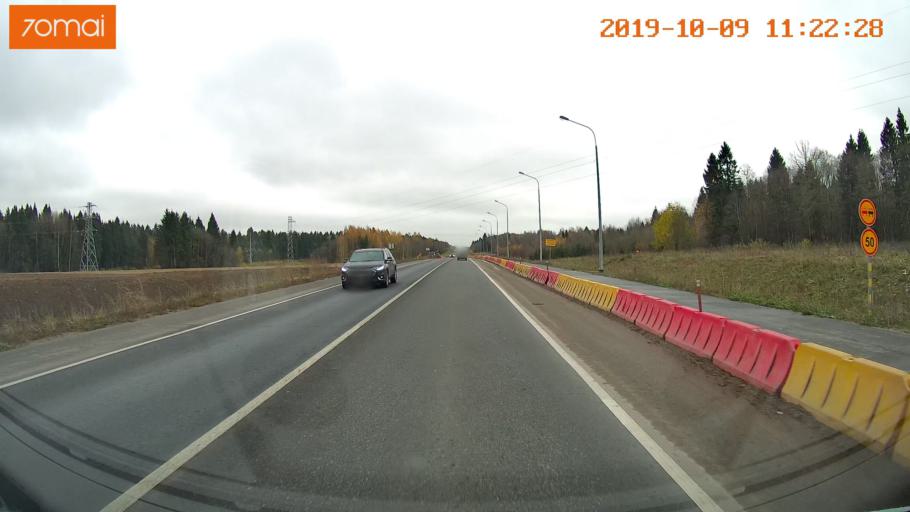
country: RU
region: Vologda
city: Vologda
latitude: 59.1315
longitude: 39.9581
